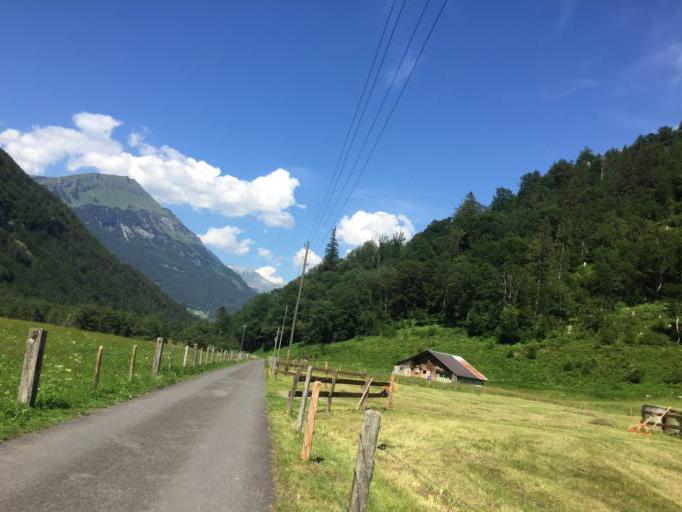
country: CH
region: Bern
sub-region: Interlaken-Oberhasli District
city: Meiringen
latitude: 46.6832
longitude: 8.2132
